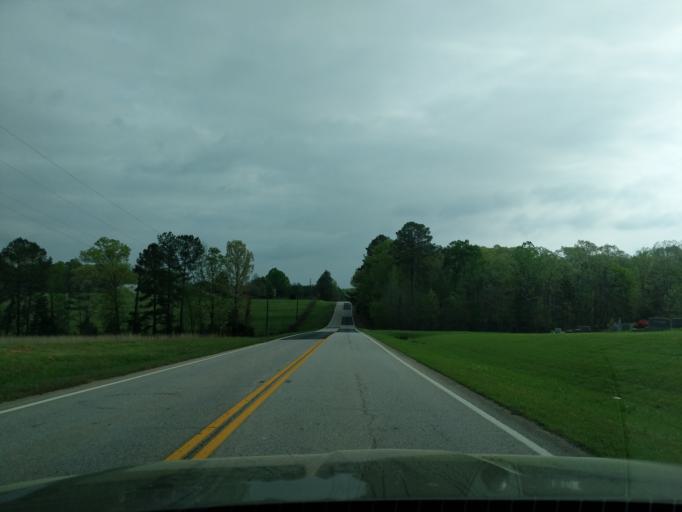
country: US
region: Georgia
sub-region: Lincoln County
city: Lincolnton
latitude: 33.7524
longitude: -82.3885
